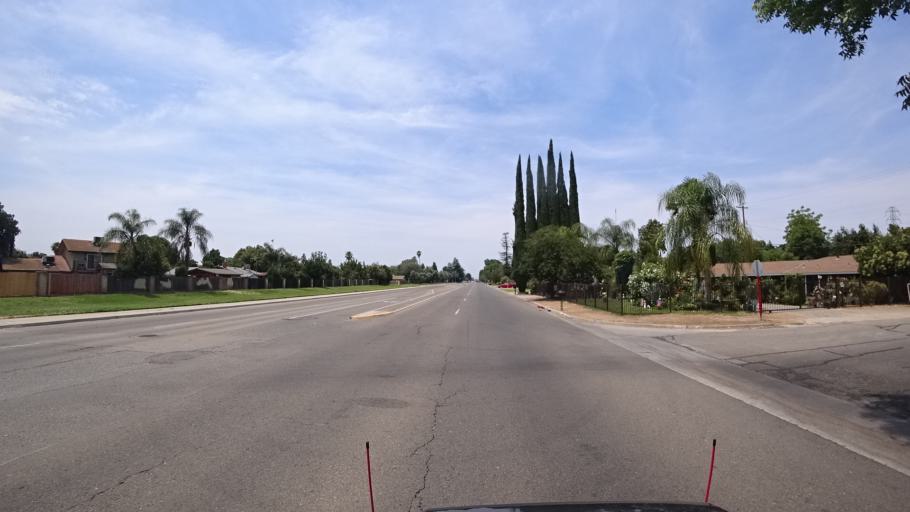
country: US
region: California
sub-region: Fresno County
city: Sunnyside
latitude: 36.7504
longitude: -119.7116
